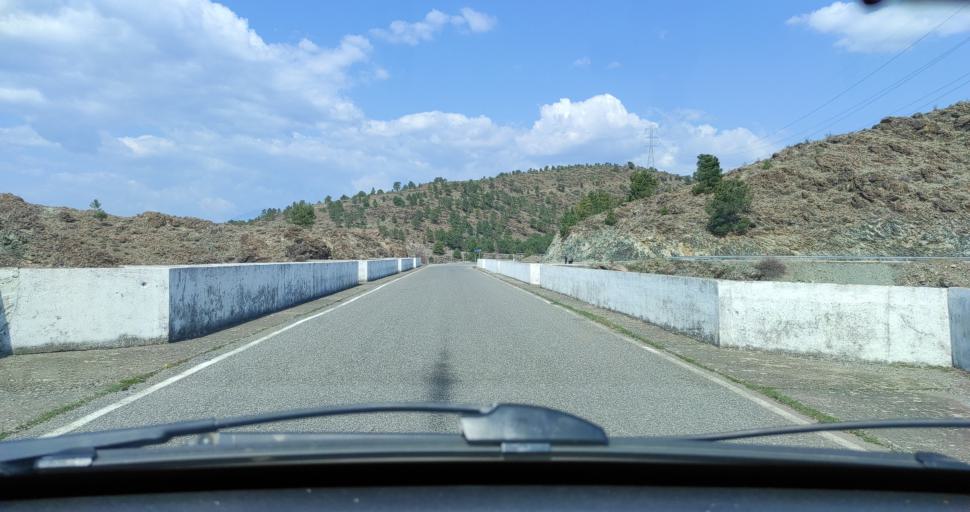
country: AL
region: Shkoder
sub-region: Rrethi i Shkodres
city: Hajmel
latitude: 41.9790
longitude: 19.6453
